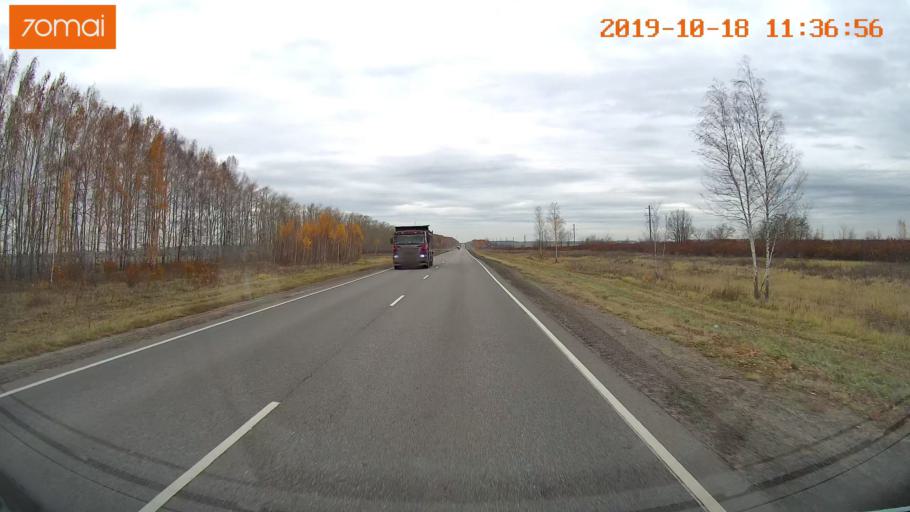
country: RU
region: Rjazan
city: Oktyabr'skiy
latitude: 54.1461
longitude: 38.8183
